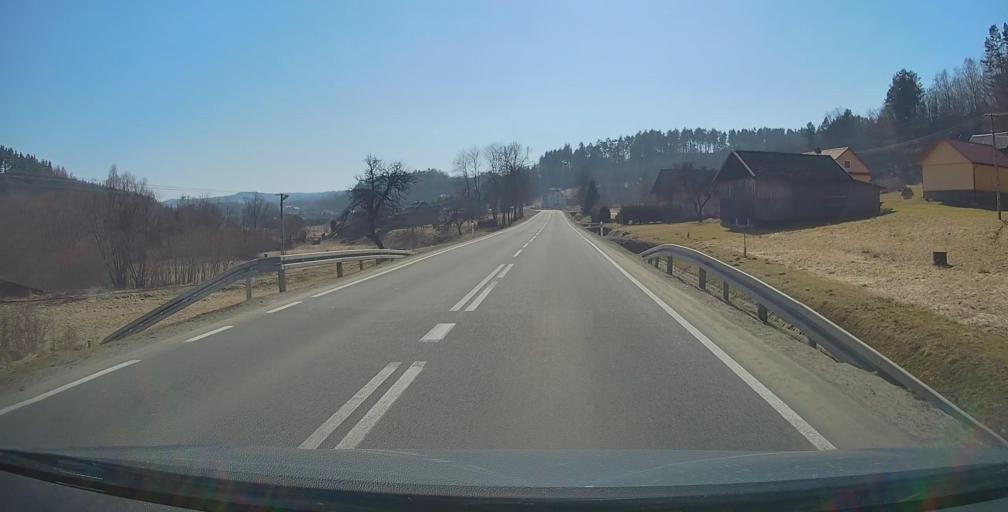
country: PL
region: Subcarpathian Voivodeship
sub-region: Powiat przemyski
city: Bircza
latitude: 49.6738
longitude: 22.4310
